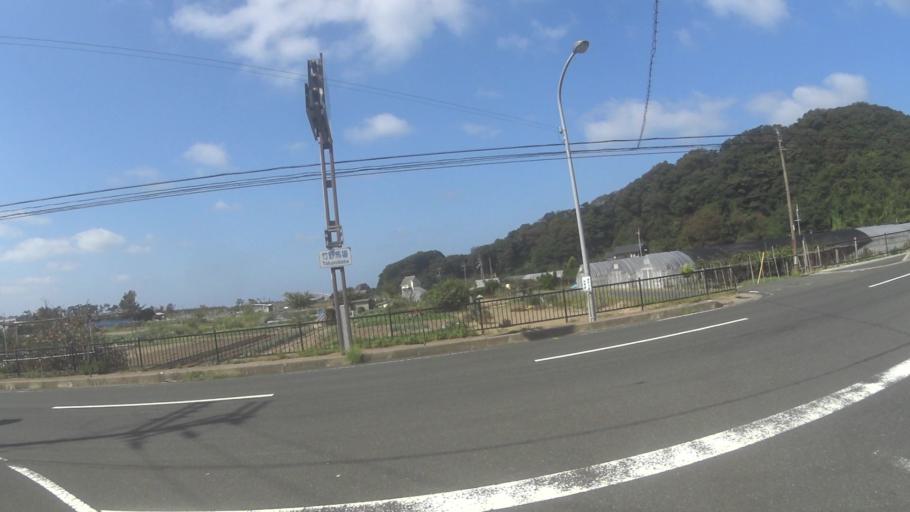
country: JP
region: Kyoto
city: Miyazu
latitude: 35.7401
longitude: 135.1097
